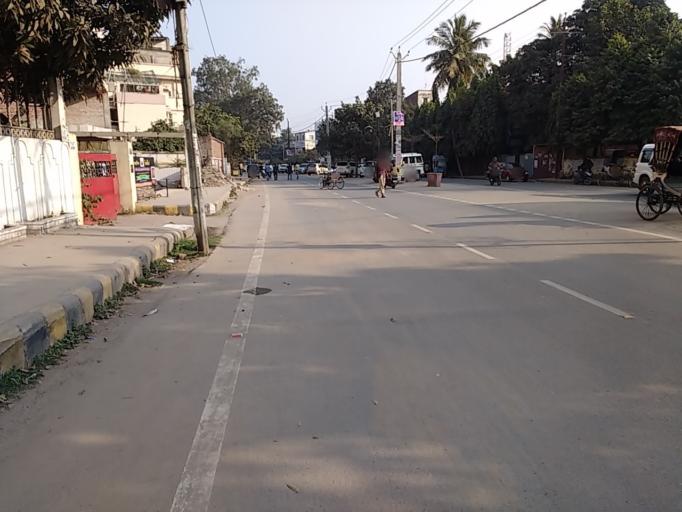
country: IN
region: Bihar
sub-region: Patna
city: Patna
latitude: 25.6122
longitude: 85.1153
